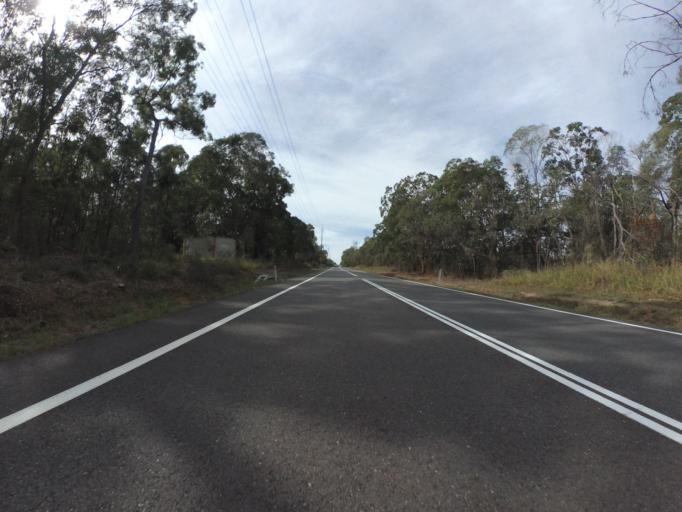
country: AU
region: Queensland
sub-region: Brisbane
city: Moggill
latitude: -27.5761
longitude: 152.8648
